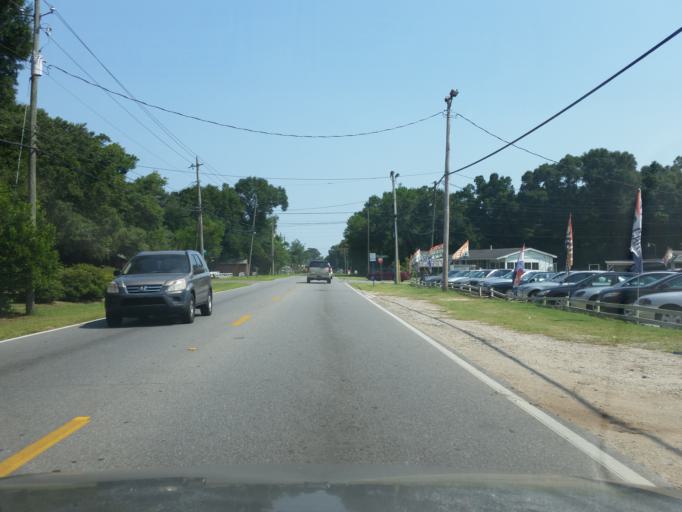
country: US
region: Florida
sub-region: Escambia County
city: Brent
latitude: 30.4941
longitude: -87.2535
